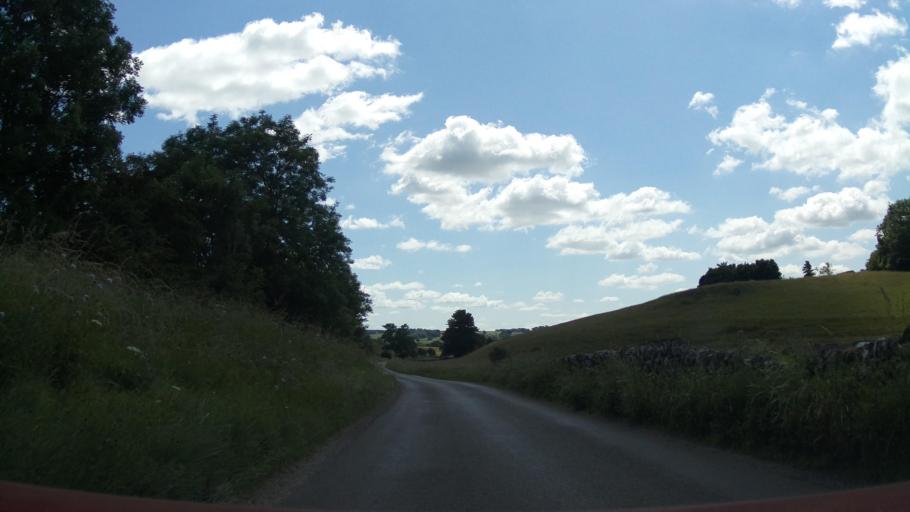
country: GB
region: England
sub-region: Derbyshire
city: Tideswell
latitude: 53.2081
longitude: -1.7807
